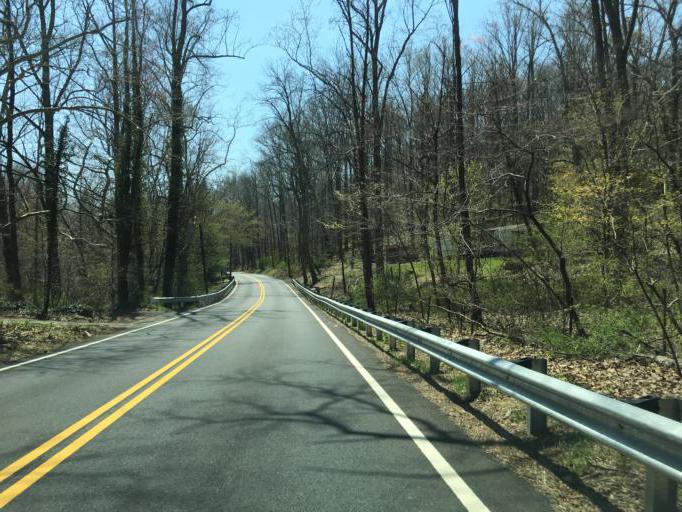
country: US
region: Maryland
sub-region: Frederick County
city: Myersville
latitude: 39.5417
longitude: -77.5300
